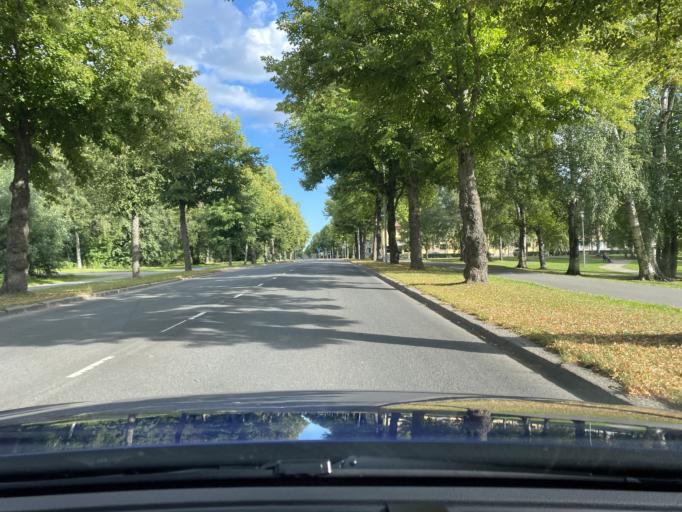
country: FI
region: Pirkanmaa
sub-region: Tampere
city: Tampere
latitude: 61.4861
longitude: 23.7932
